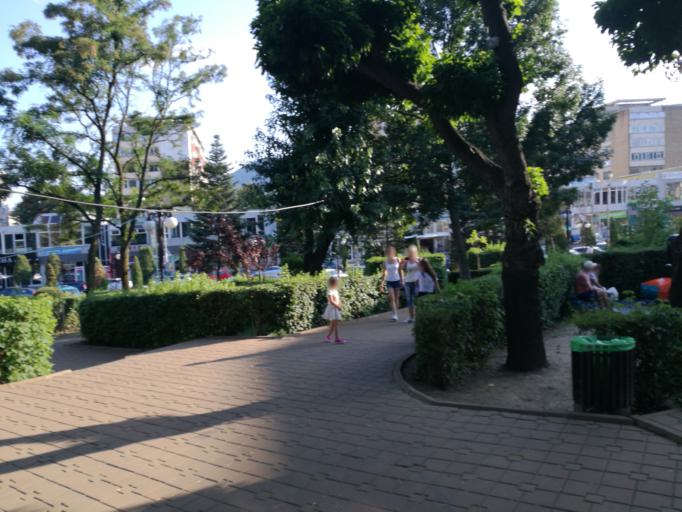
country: RO
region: Neamt
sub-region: Municipiul Piatra-Neamt
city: Valeni
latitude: 46.9324
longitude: 26.3689
